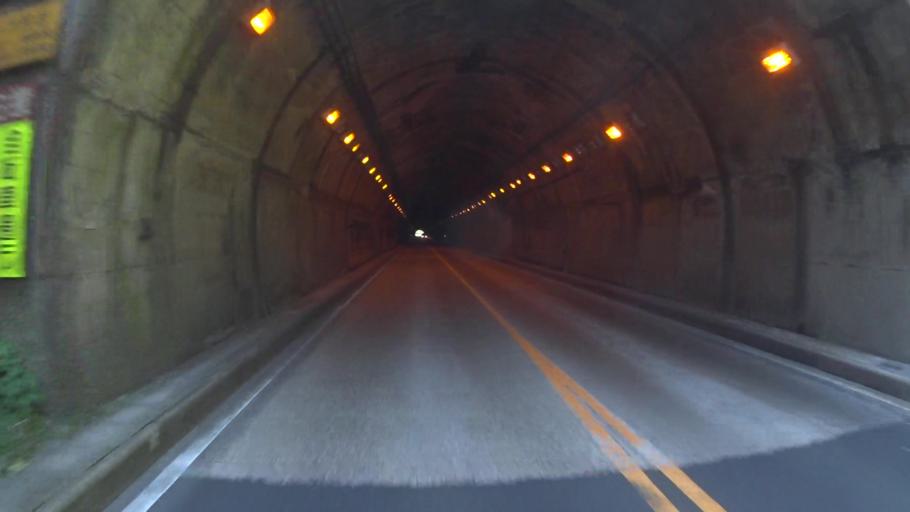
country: JP
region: Kyoto
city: Miyazu
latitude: 35.5518
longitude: 135.2233
